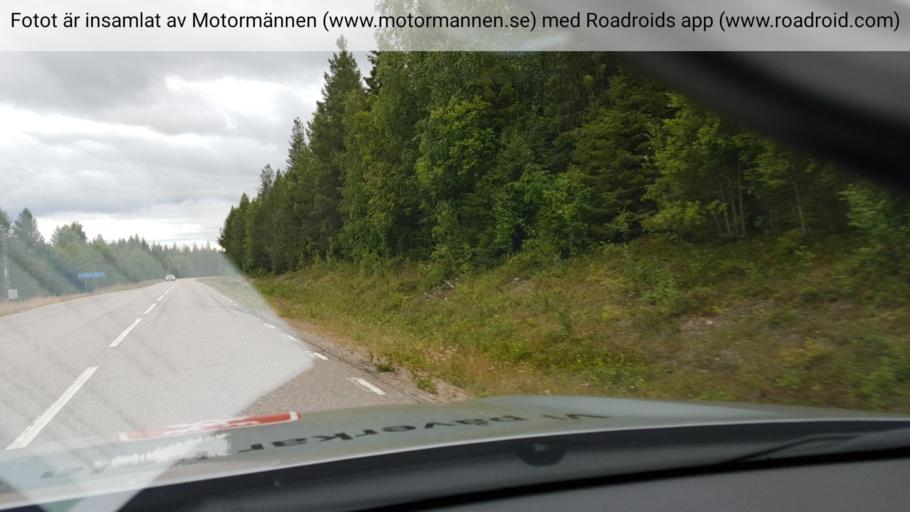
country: SE
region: Norrbotten
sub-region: Overkalix Kommun
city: OEverkalix
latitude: 66.6896
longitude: 22.8986
